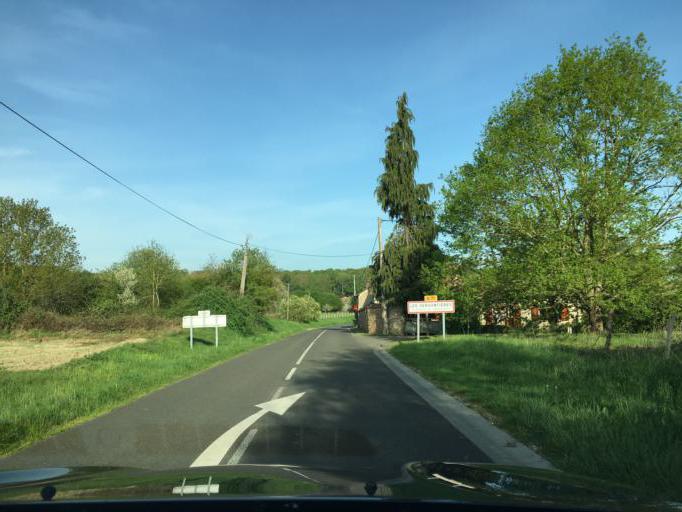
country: FR
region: Ile-de-France
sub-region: Departement des Yvelines
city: Conde-sur-Vesgre
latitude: 48.7162
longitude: 1.6605
